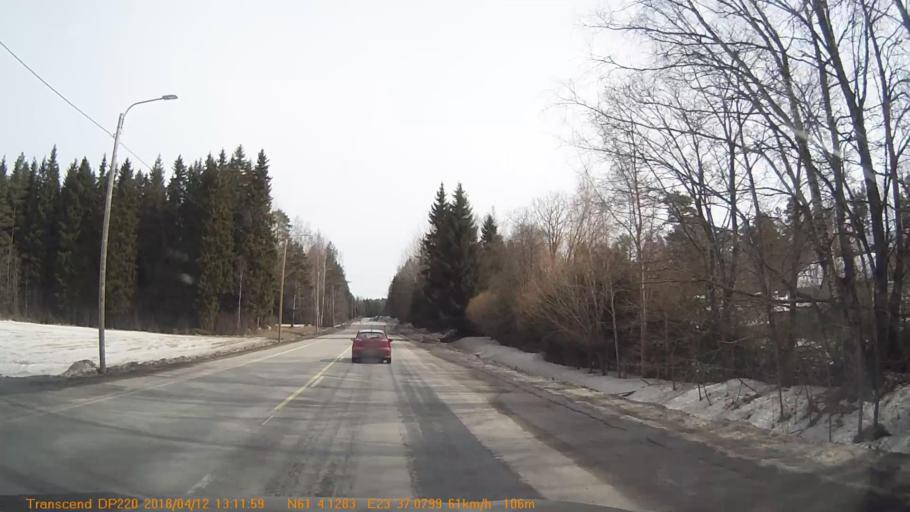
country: FI
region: Pirkanmaa
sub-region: Etelae-Pirkanmaa
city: Urjala
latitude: 61.0687
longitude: 23.6195
